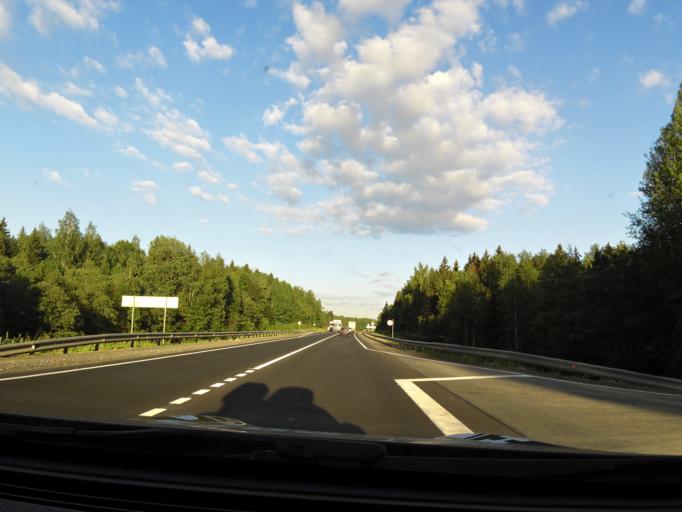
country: RU
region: Vologda
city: Gryazovets
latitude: 59.0485
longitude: 40.0890
